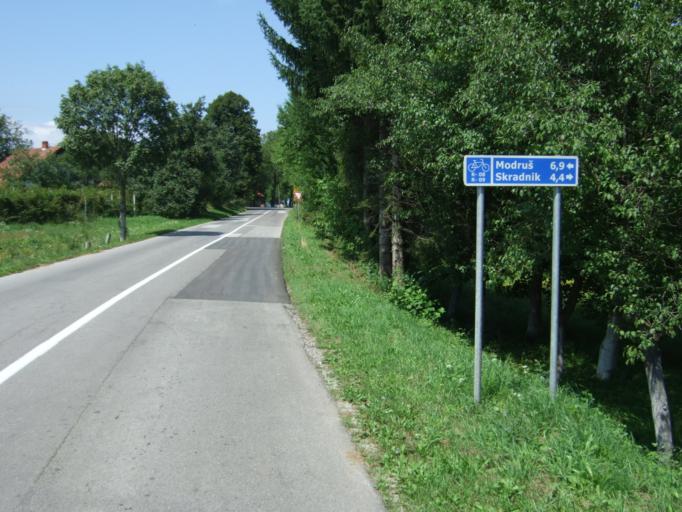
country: HR
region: Karlovacka
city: Ostarije
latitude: 45.1783
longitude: 15.2890
